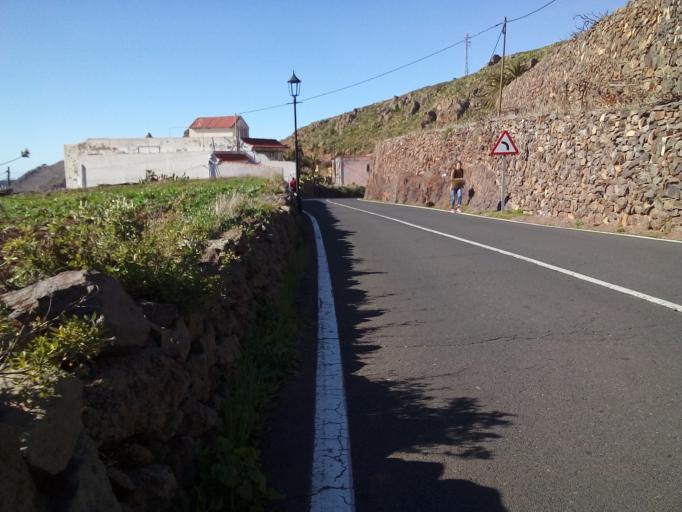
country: ES
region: Canary Islands
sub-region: Provincia de Santa Cruz de Tenerife
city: Vallehermosa
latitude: 28.1335
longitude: -17.3212
